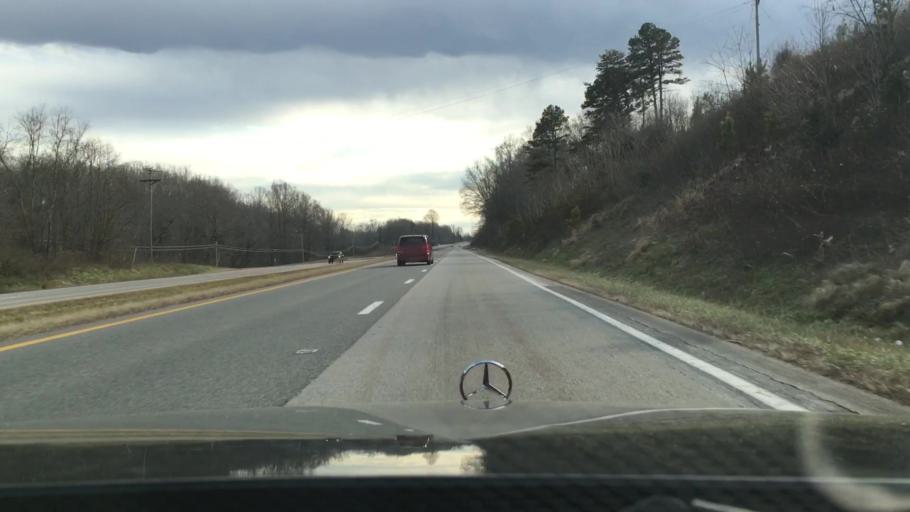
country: US
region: Virginia
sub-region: Pittsylvania County
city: Motley
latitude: 37.0144
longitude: -79.3573
